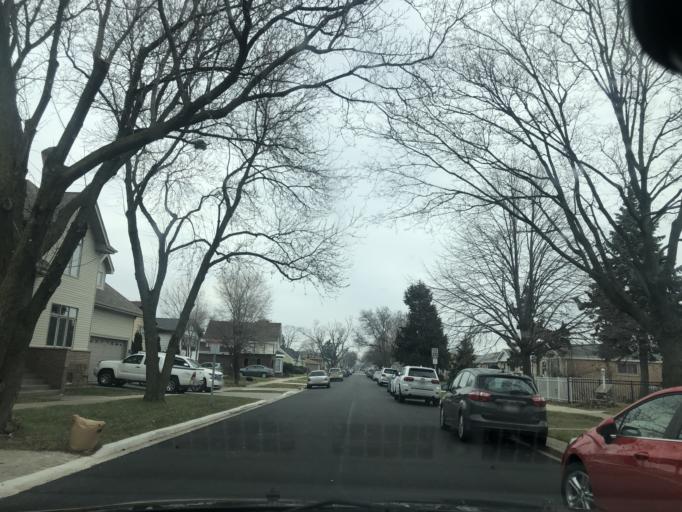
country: US
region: Illinois
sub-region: Cook County
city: Schiller Park
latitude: 41.9714
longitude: -87.8674
